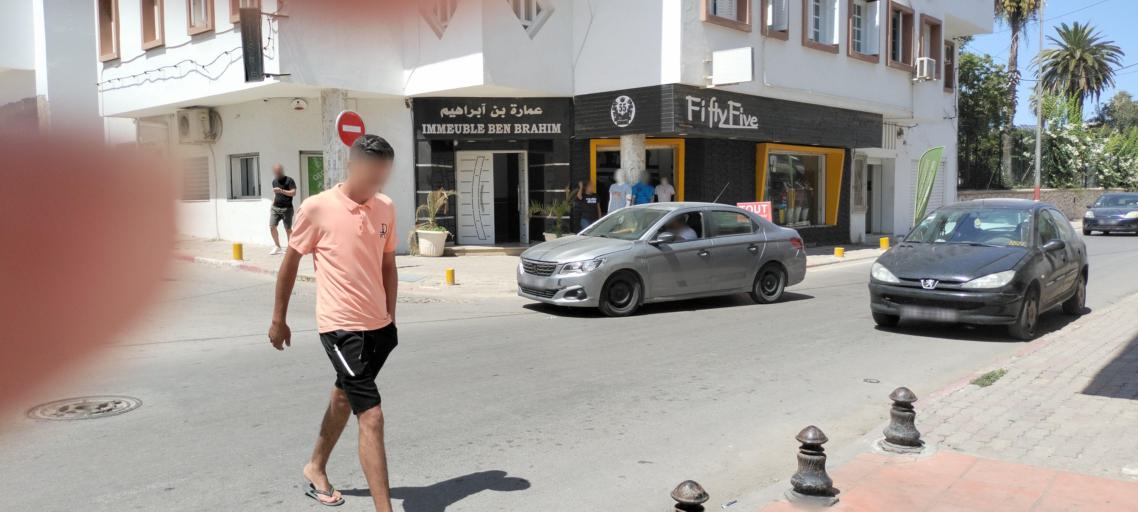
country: TN
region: Susah
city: Sousse
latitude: 35.8315
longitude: 10.6396
